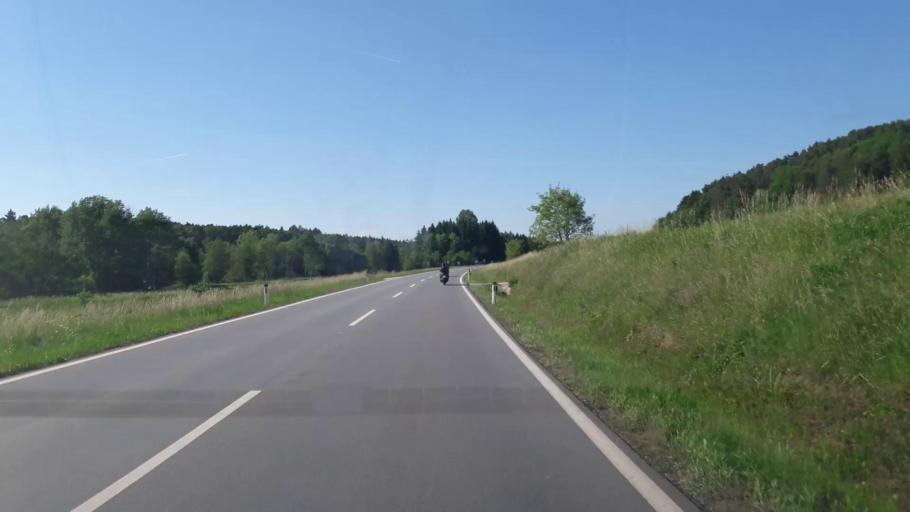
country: AT
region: Burgenland
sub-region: Politischer Bezirk Gussing
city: Ollersdorf im Burgenland
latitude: 47.1925
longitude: 16.1616
